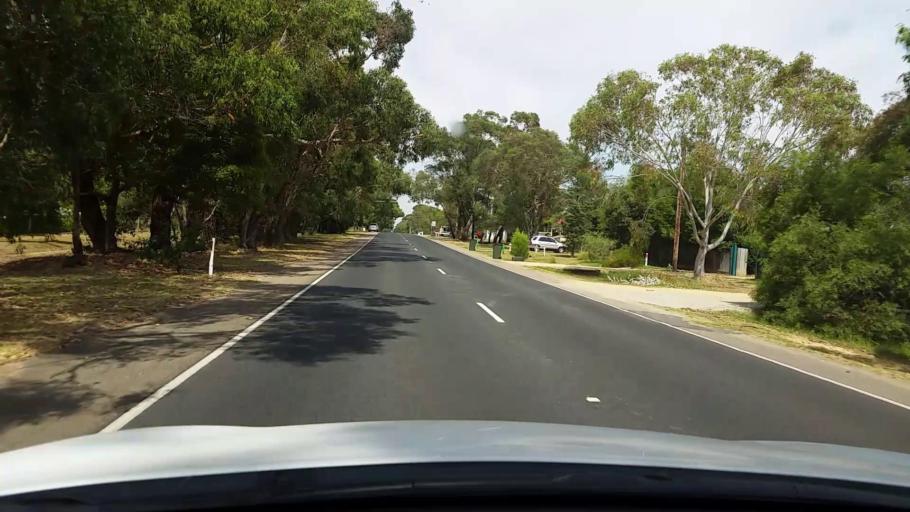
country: AU
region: Victoria
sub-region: Mornington Peninsula
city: Crib Point
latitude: -38.3425
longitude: 145.1711
